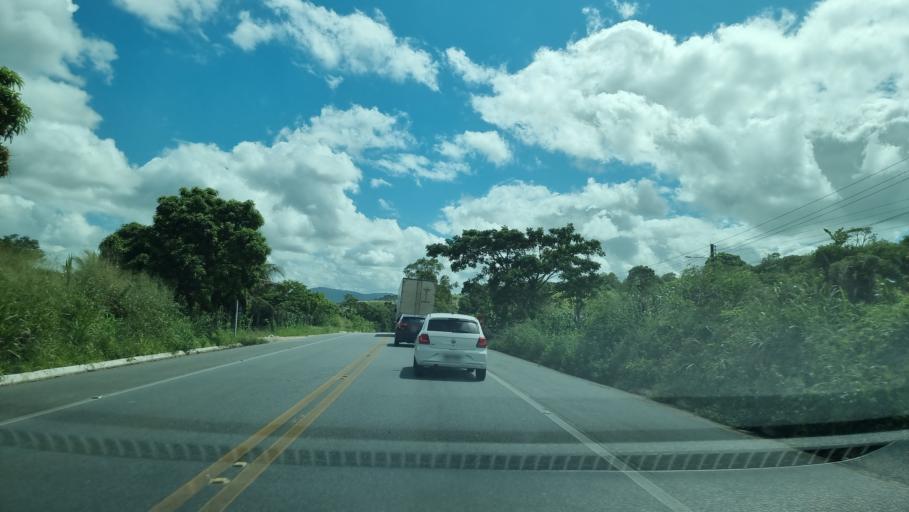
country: BR
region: Alagoas
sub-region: Uniao Dos Palmares
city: Uniao dos Palmares
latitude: -9.2241
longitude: -36.0283
